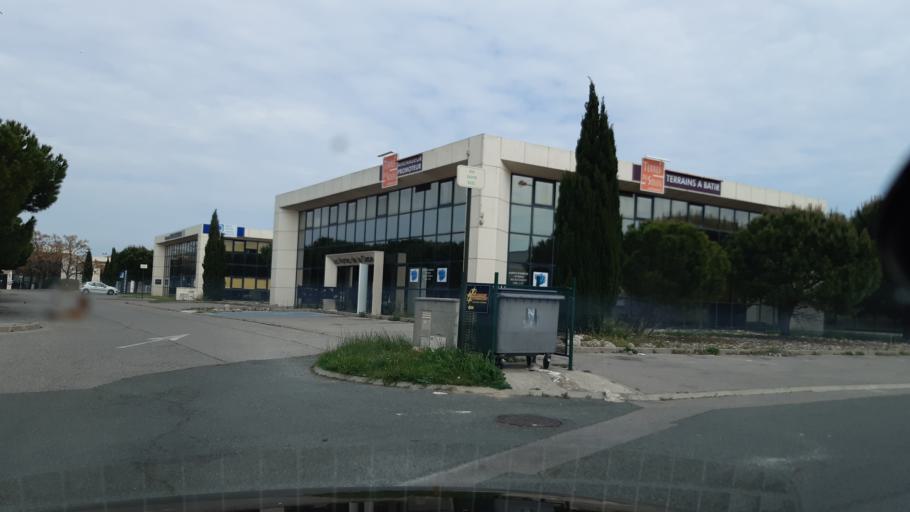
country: FR
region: Languedoc-Roussillon
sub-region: Departement de l'Aude
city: Narbonne
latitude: 43.1800
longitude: 3.0321
